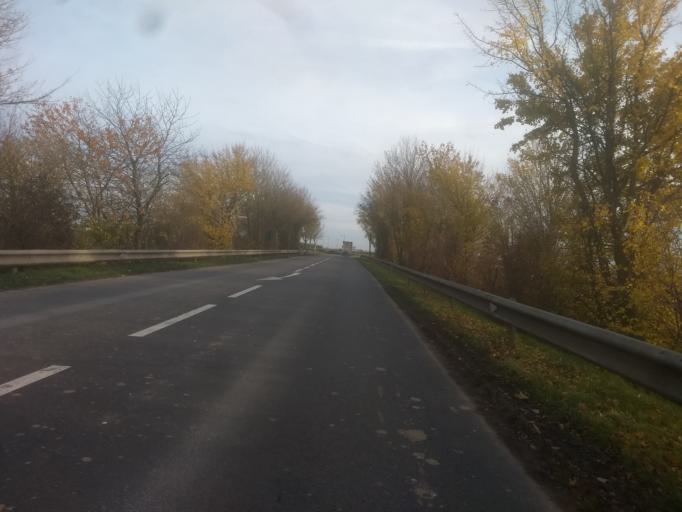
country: FR
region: Nord-Pas-de-Calais
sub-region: Departement du Pas-de-Calais
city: Agny
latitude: 50.2540
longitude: 2.7669
